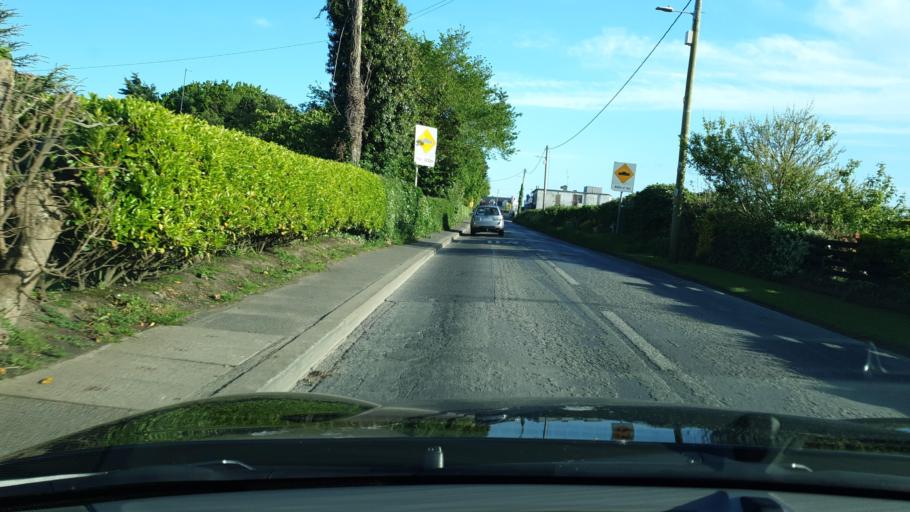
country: IE
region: Leinster
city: An Ros
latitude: 53.5489
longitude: -6.1016
